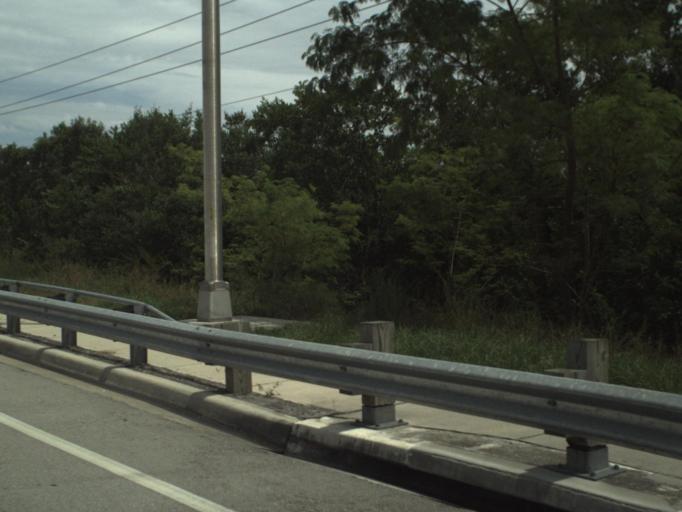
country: US
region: Florida
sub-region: Palm Beach County
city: Jupiter
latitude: 26.9365
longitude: -80.0822
